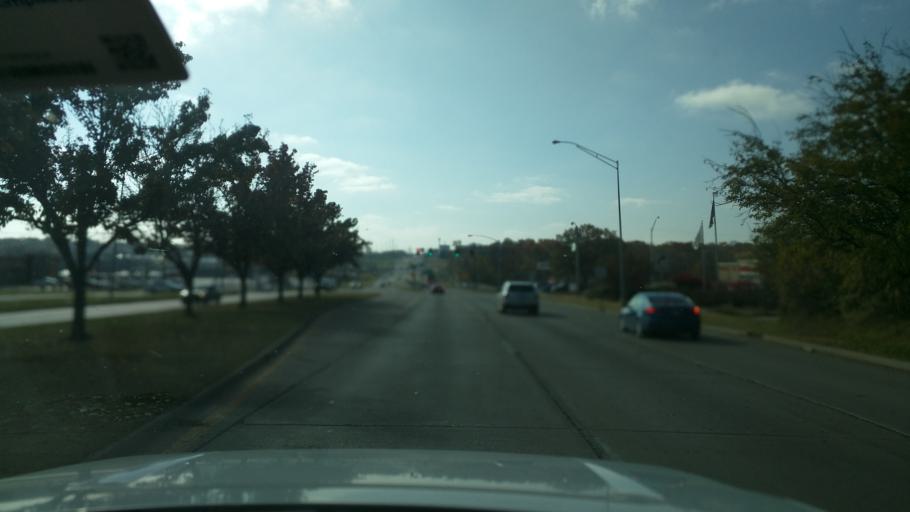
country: US
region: Oklahoma
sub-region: Washington County
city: Dewey
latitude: 36.7516
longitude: -95.9356
